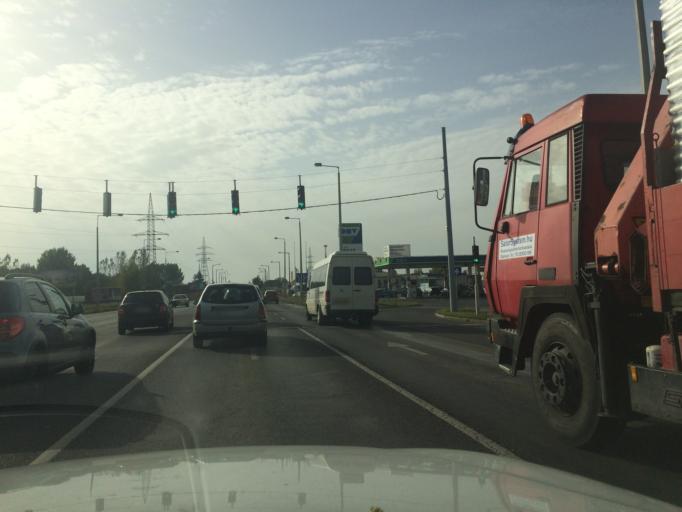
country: HU
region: Szabolcs-Szatmar-Bereg
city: Nyiregyhaza
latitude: 47.9368
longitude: 21.7188
